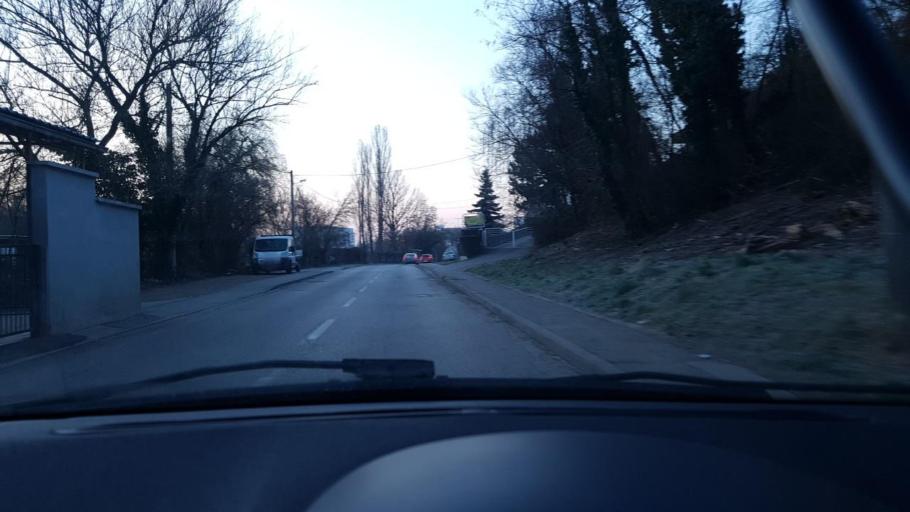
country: HR
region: Grad Zagreb
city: Zagreb
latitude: 45.8296
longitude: 16.0057
